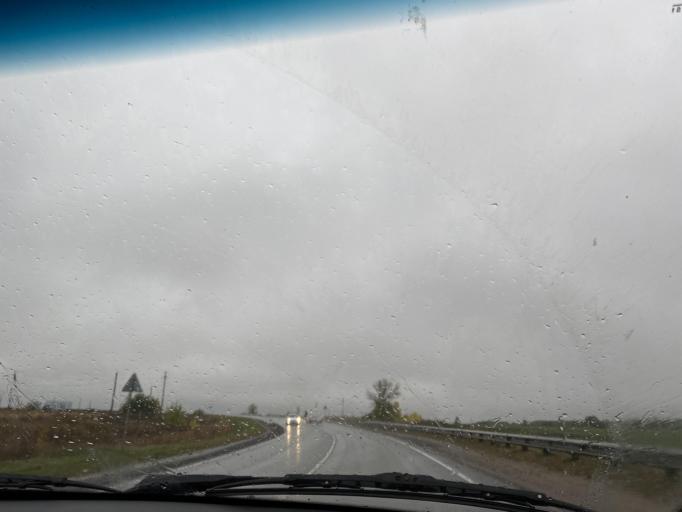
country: RU
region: Rjazan
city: Ryazan'
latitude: 54.4845
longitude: 39.8266
